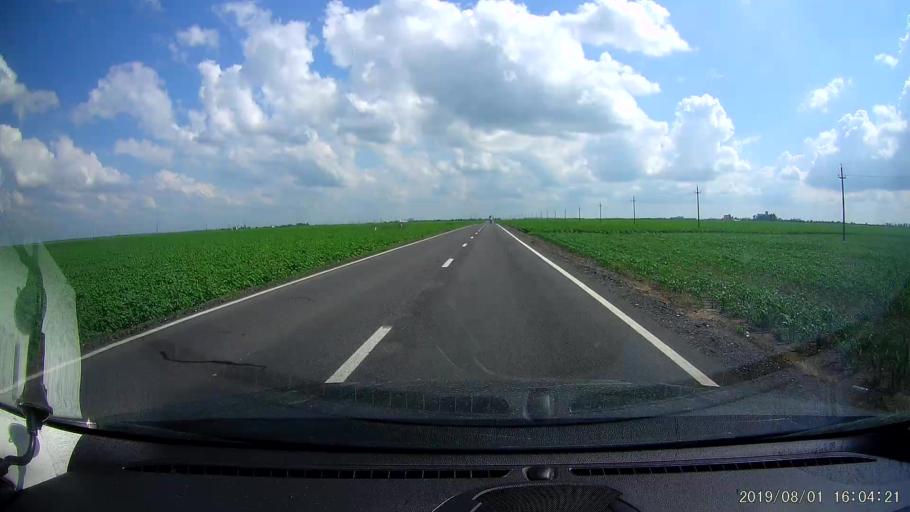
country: RO
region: Calarasi
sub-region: Comuna Dragalina
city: Drajna Noua
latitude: 44.4498
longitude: 27.3805
